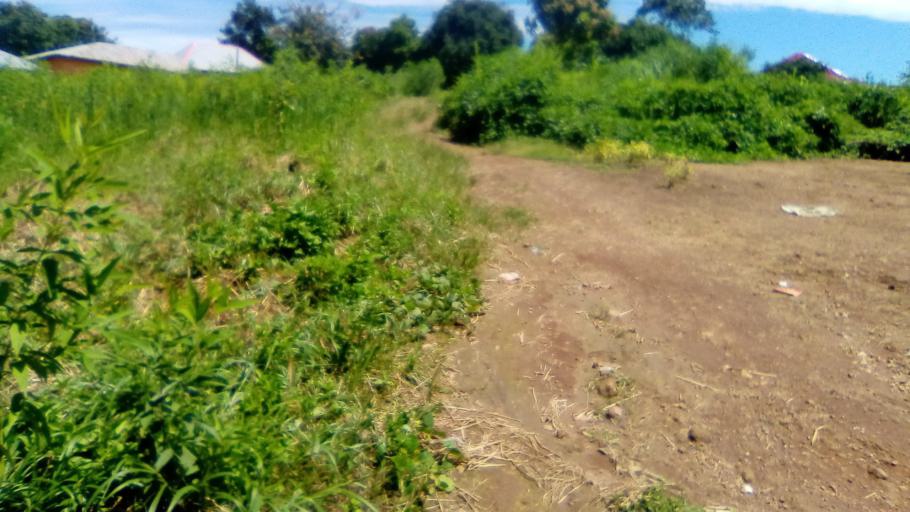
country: SL
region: Eastern Province
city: Simbakoro
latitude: 8.6303
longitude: -10.9953
